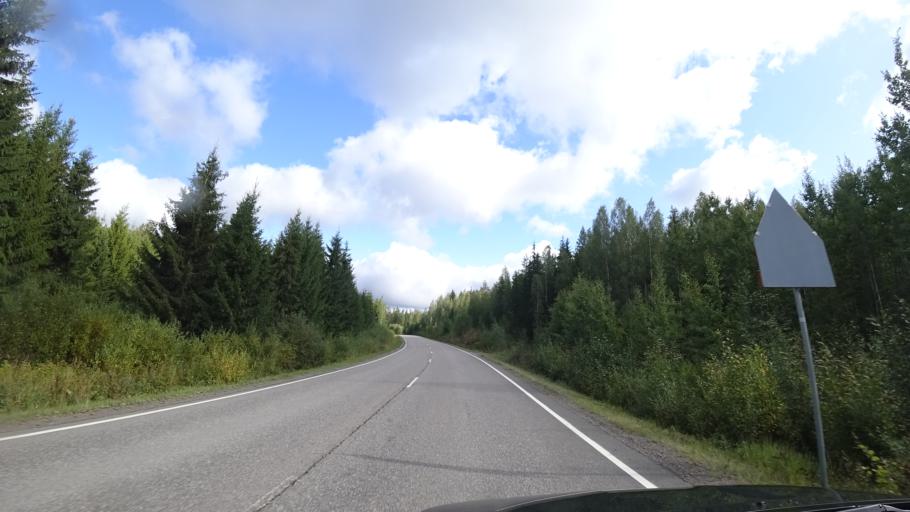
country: FI
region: Uusimaa
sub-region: Helsinki
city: Hyvinge
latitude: 60.6309
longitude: 25.0095
